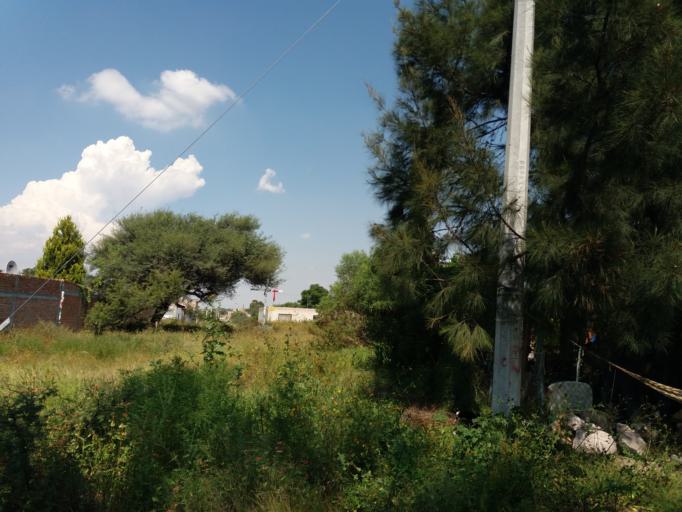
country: MX
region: Aguascalientes
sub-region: Aguascalientes
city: Penuelas (El Cienegal)
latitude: 21.7513
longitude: -102.3043
